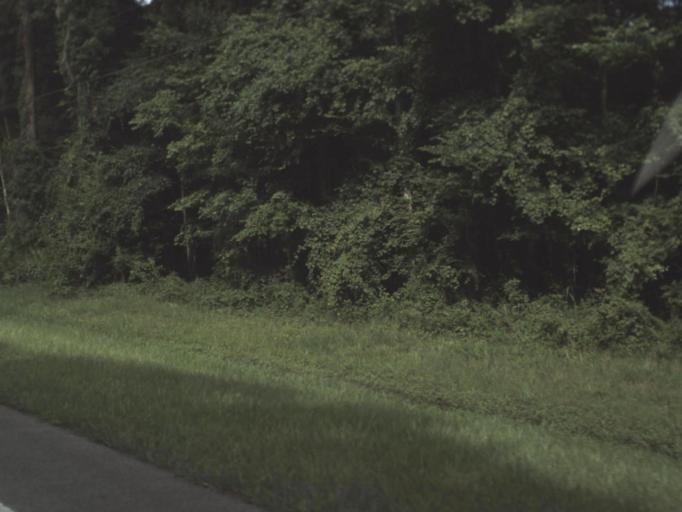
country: US
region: Florida
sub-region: Hernando County
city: Ridge Manor
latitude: 28.5155
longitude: -82.1041
